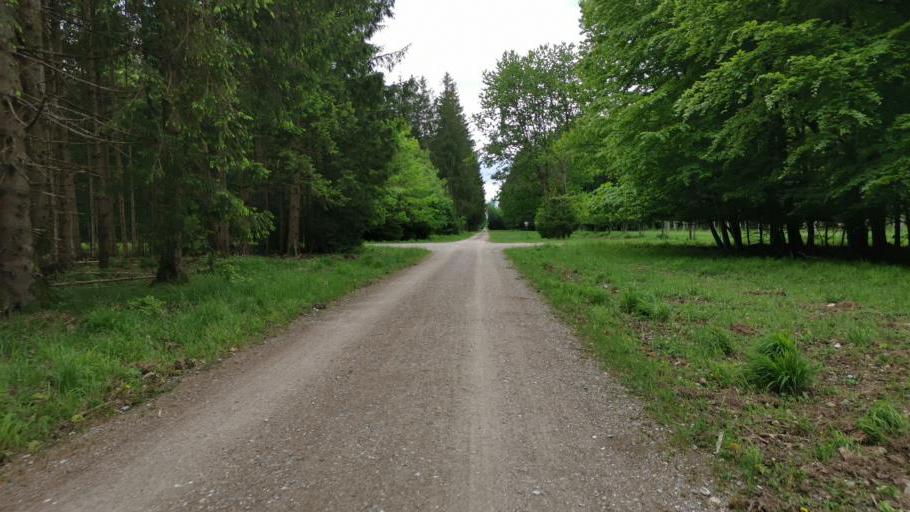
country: DE
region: Bavaria
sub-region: Upper Bavaria
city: Pullach im Isartal
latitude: 48.0562
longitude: 11.4924
